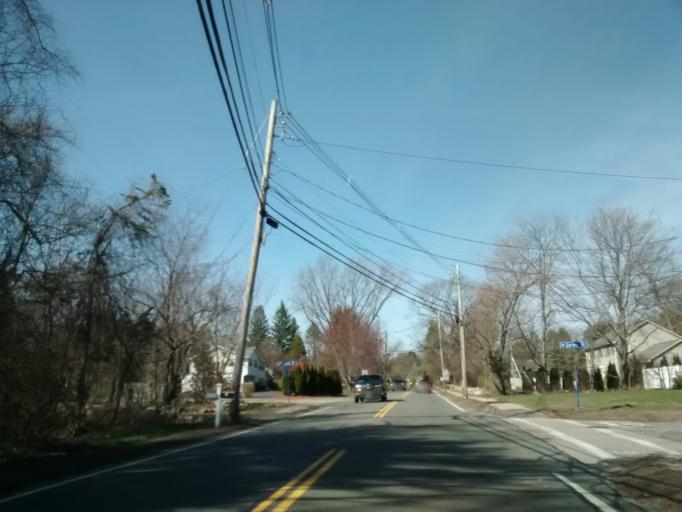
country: US
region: Massachusetts
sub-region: Norfolk County
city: Medway
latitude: 42.1557
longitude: -71.4090
